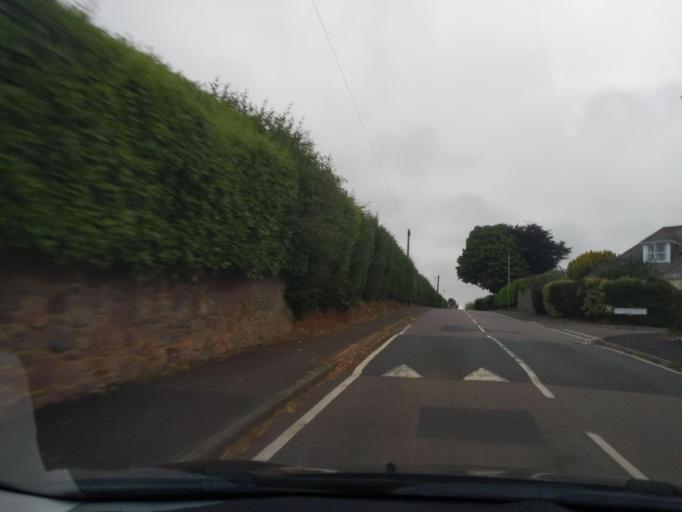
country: GB
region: England
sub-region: Devon
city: Marldon
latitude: 50.4530
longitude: -3.5938
